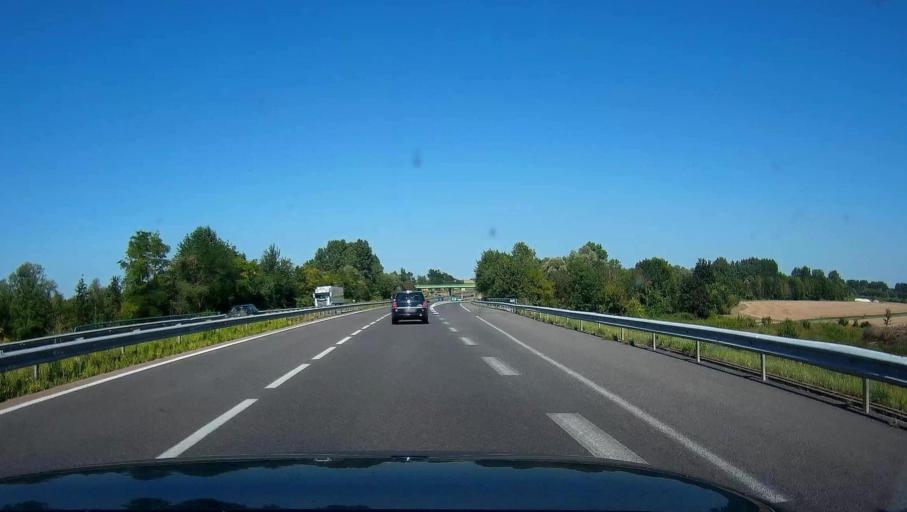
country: FR
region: Champagne-Ardenne
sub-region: Departement de la Marne
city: Fagnieres
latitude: 48.9671
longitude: 4.2841
